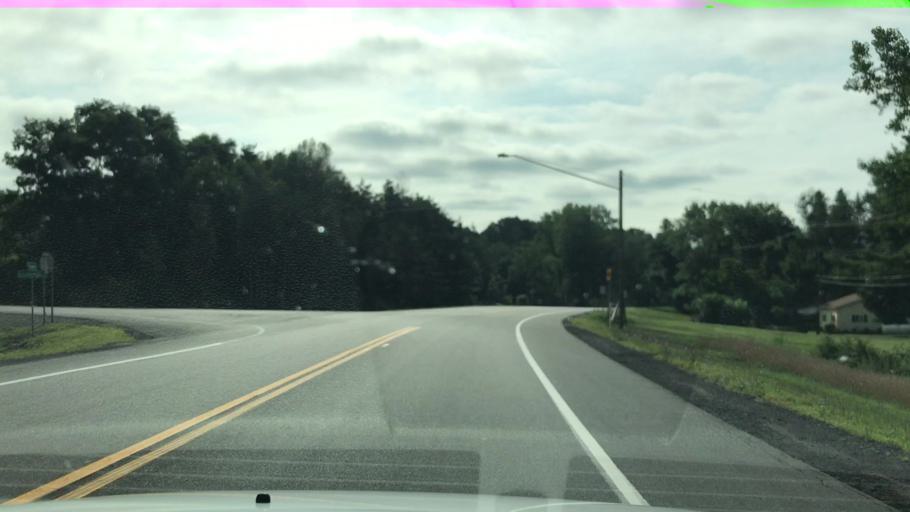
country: US
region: New York
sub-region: Erie County
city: Alden
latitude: 42.8572
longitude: -78.4995
